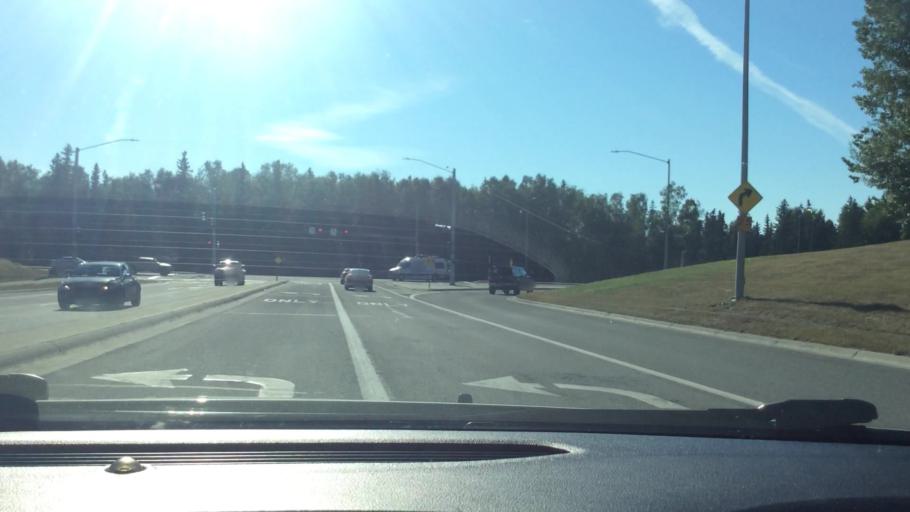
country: US
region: Alaska
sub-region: Anchorage Municipality
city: Anchorage
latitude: 61.2333
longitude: -149.7765
